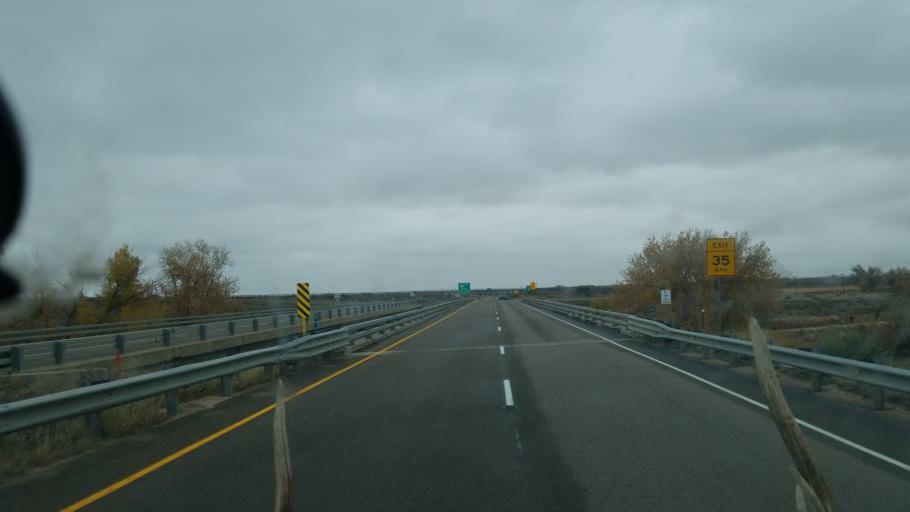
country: US
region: Colorado
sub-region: Pueblo County
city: Pueblo
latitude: 38.2658
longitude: -104.3733
